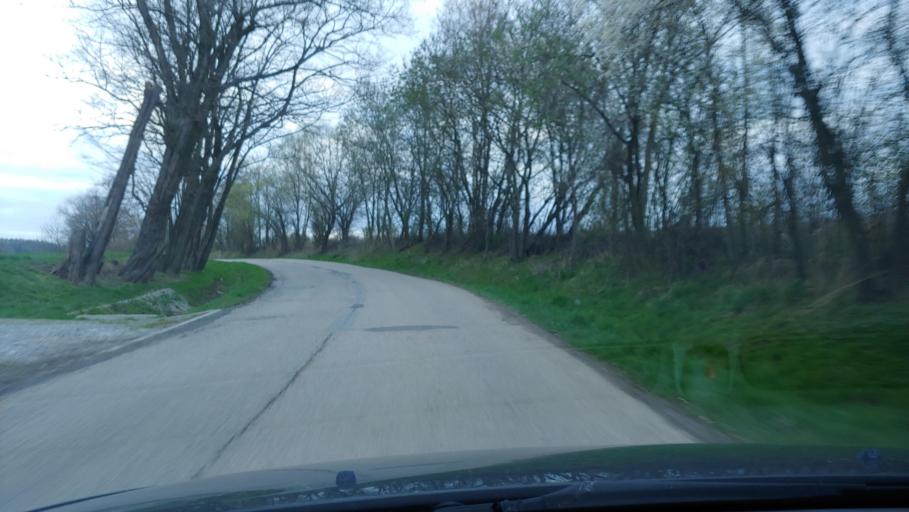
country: PL
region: Lesser Poland Voivodeship
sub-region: Powiat krakowski
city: Rudawa
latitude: 50.1381
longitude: 19.7514
